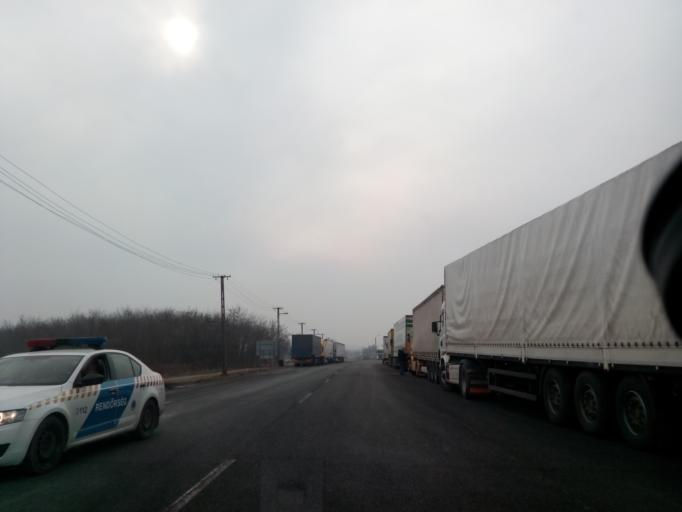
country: HU
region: Borsod-Abauj-Zemplen
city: Gonc
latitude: 48.5304
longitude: 21.2539
